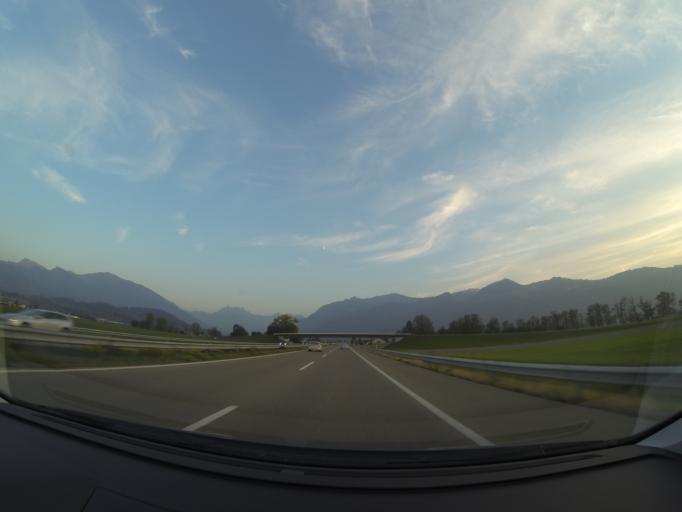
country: CH
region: Schwyz
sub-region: Bezirk March
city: Tuggen
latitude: 47.1988
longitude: 8.9692
